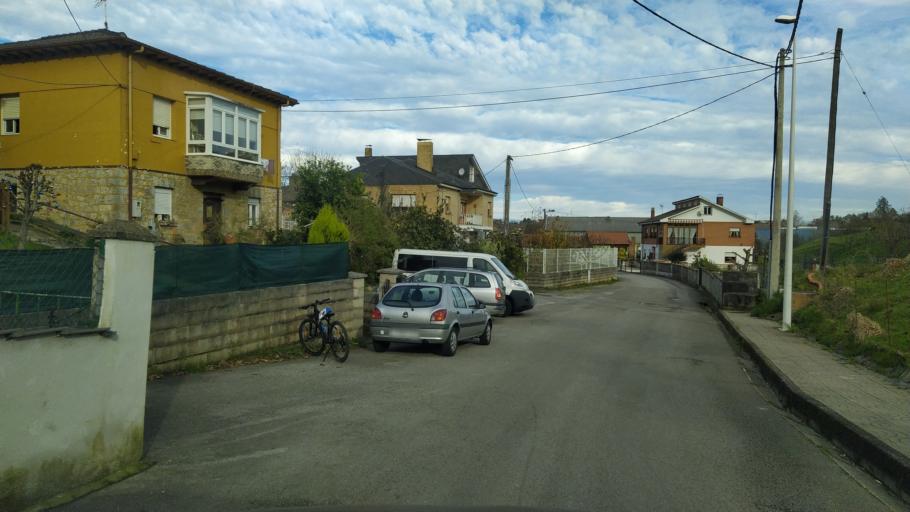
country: ES
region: Cantabria
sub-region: Provincia de Cantabria
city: Reocin
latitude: 43.3555
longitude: -4.0882
